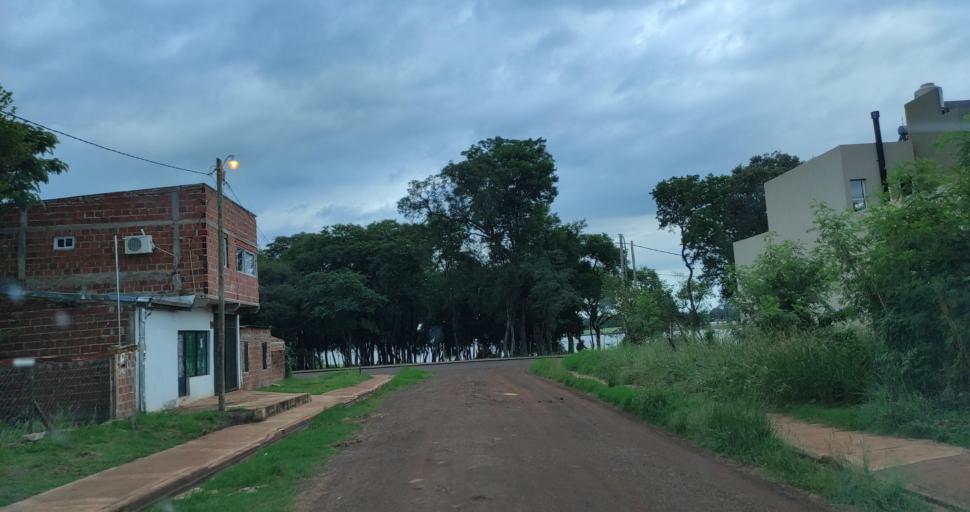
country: AR
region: Misiones
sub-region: Departamento de Capital
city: Posadas
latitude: -27.3629
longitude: -55.9453
